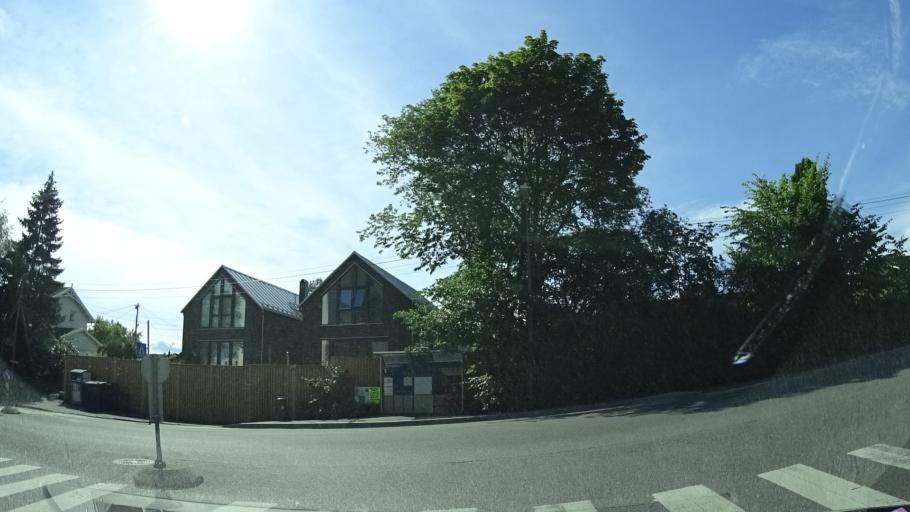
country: NO
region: Oslo
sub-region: Oslo
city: Oslo
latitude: 59.9596
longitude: 10.7646
